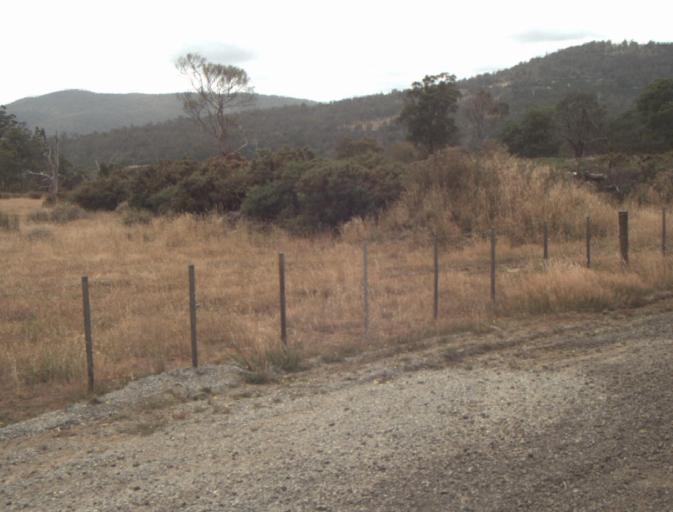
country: AU
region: Tasmania
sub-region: Northern Midlands
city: Evandale
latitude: -41.5197
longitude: 147.3750
